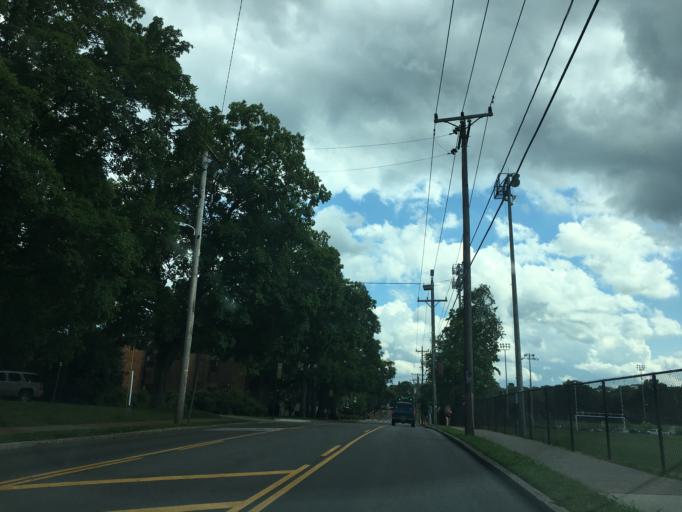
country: US
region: Tennessee
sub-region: Davidson County
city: Nashville
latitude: 36.1407
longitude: -86.8069
